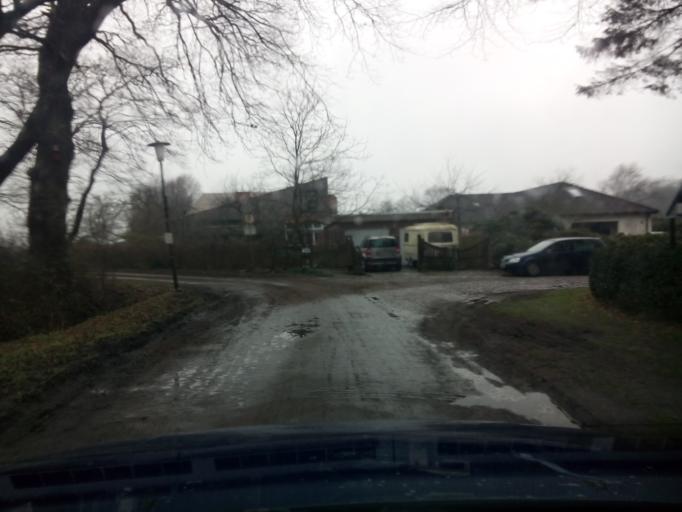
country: DE
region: Lower Saxony
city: Osterholz-Scharmbeck
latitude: 53.2485
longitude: 8.7971
